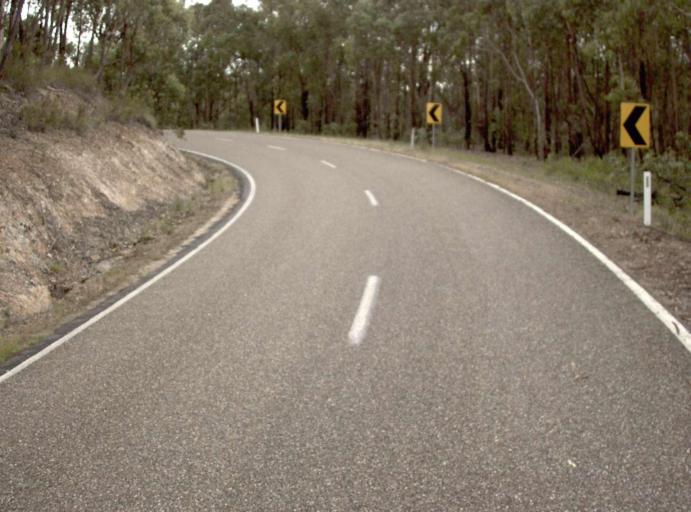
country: AU
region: Victoria
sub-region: East Gippsland
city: Bairnsdale
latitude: -37.6532
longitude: 147.2769
